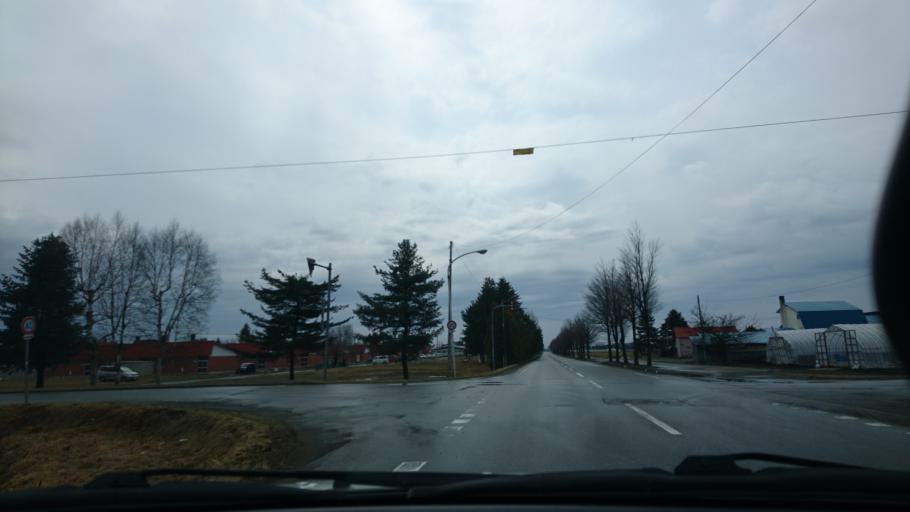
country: JP
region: Hokkaido
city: Otofuke
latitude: 42.9765
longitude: 143.1913
